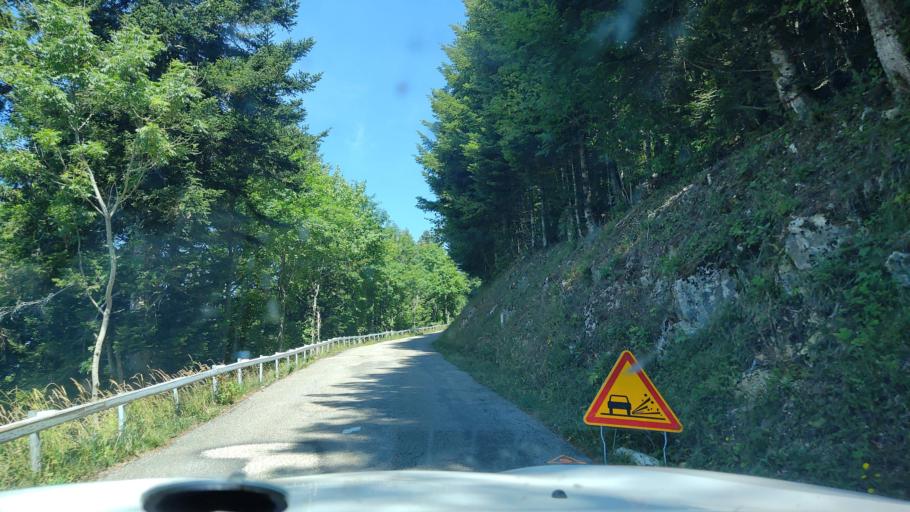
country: FR
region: Rhone-Alpes
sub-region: Departement de la Savoie
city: Le Bourget-du-Lac
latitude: 45.6512
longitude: 5.8092
